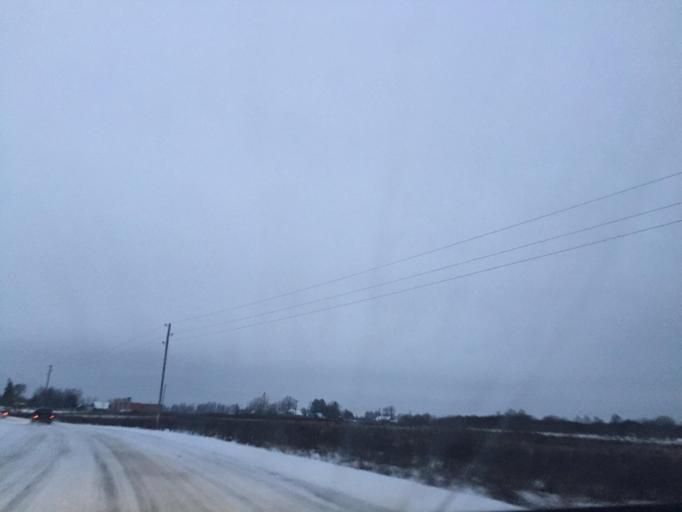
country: LV
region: Raunas
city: Rauna
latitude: 57.4307
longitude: 25.6303
